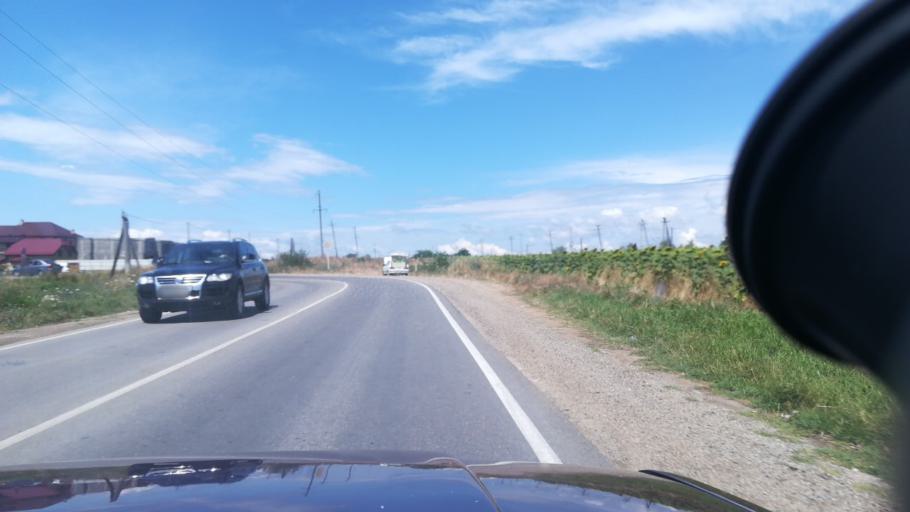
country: RU
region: Krasnodarskiy
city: Tsibanobalka
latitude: 44.9615
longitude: 37.3034
